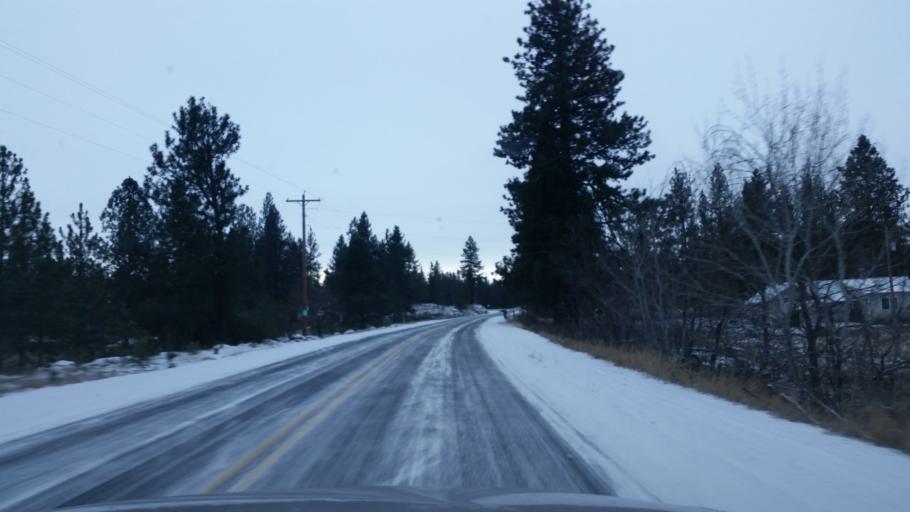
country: US
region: Washington
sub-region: Spokane County
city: Cheney
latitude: 47.4302
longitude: -117.5096
